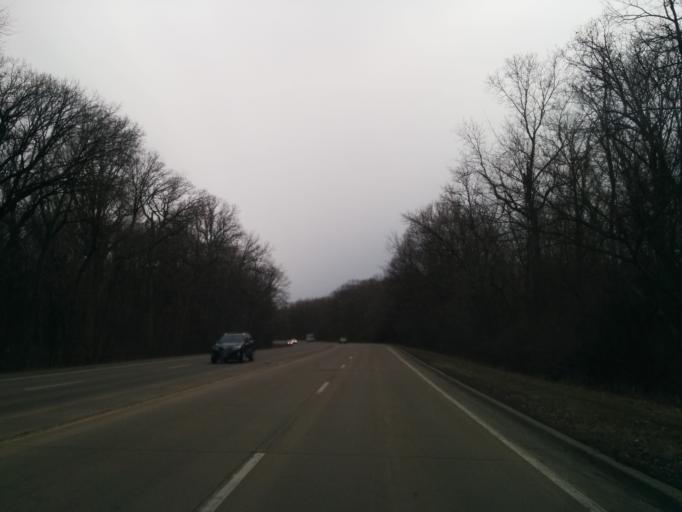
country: US
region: Illinois
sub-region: Cook County
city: Des Plaines
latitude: 42.0875
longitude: -87.8814
